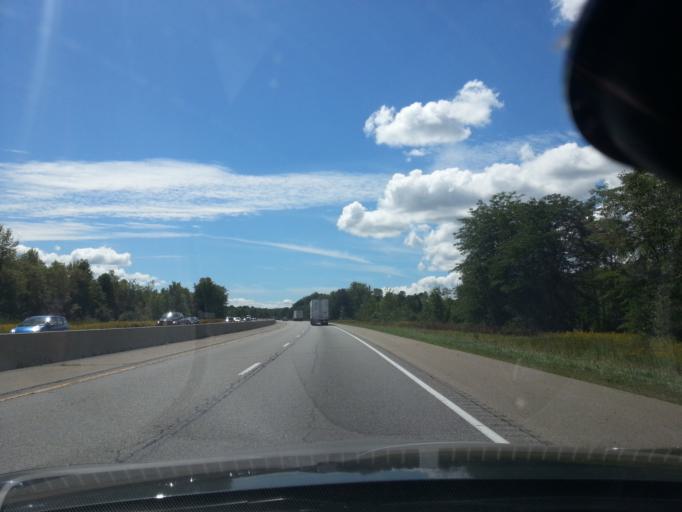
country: CA
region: Ontario
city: Brockville
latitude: 44.6408
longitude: -75.6433
